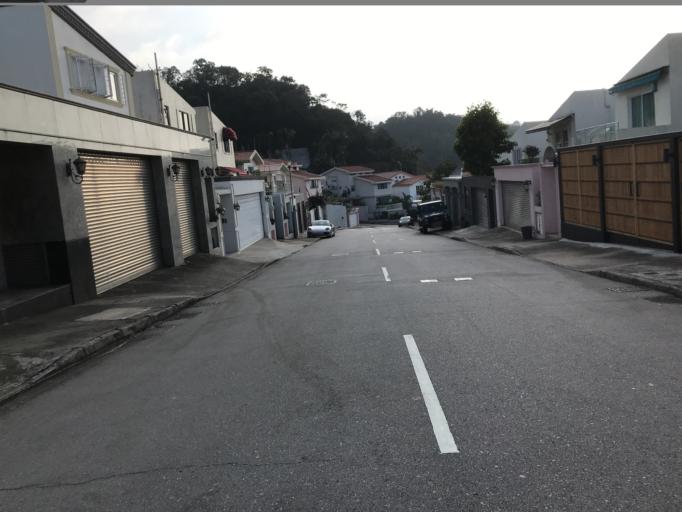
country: HK
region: Tai Po
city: Tai Po
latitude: 22.4627
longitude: 114.1591
